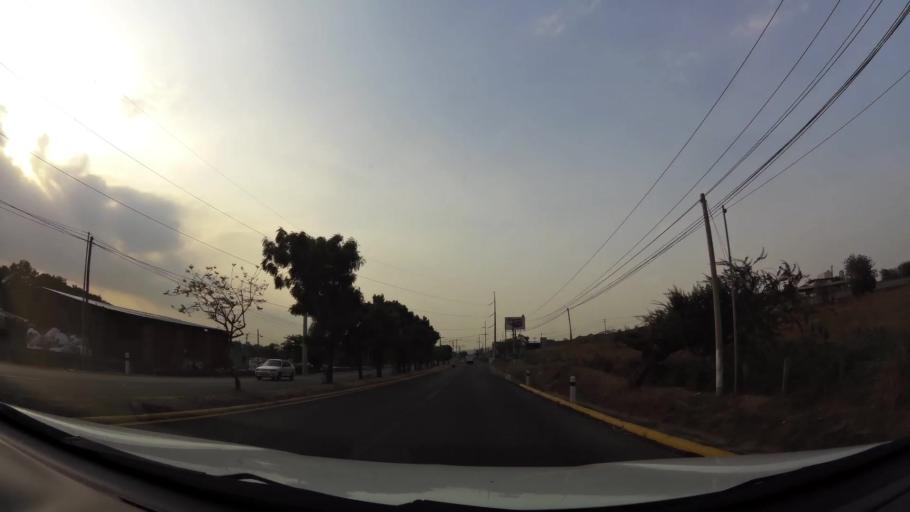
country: NI
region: Managua
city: Ciudad Sandino
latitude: 12.1532
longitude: -86.3373
